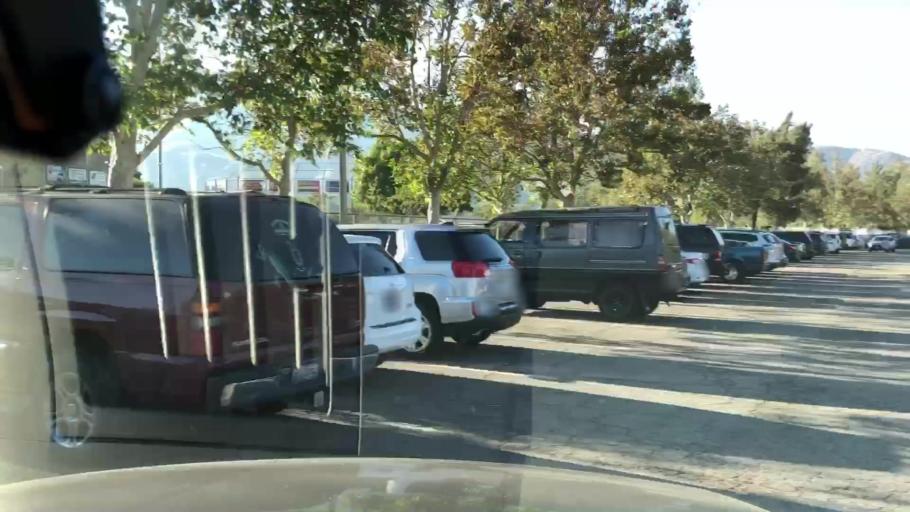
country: US
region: California
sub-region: Ventura County
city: Fillmore
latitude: 34.4031
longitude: -118.9291
